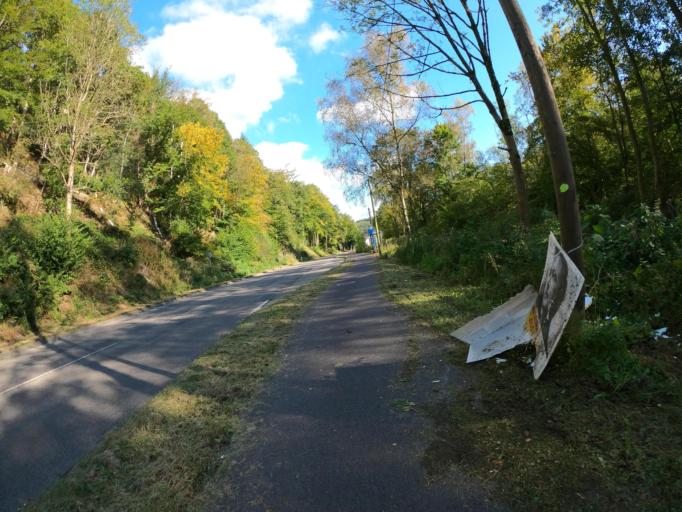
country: DE
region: North Rhine-Westphalia
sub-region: Regierungsbezirk Arnsberg
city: Schwelm
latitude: 51.2557
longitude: 7.2611
